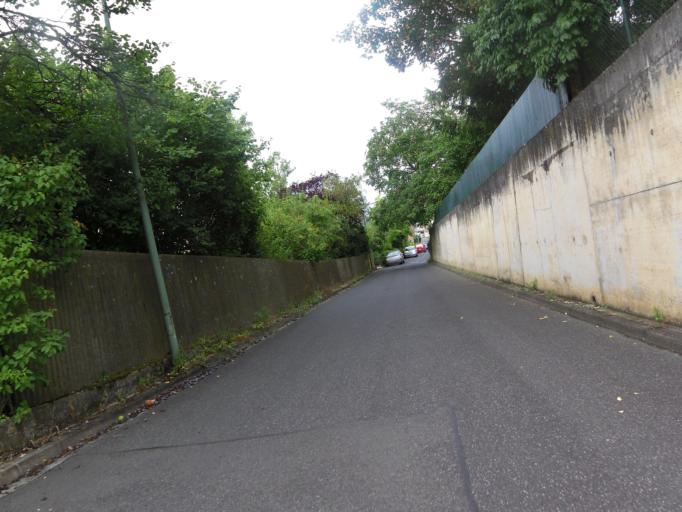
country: DE
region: Bavaria
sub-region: Regierungsbezirk Unterfranken
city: Hochberg
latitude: 49.7836
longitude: 9.8875
